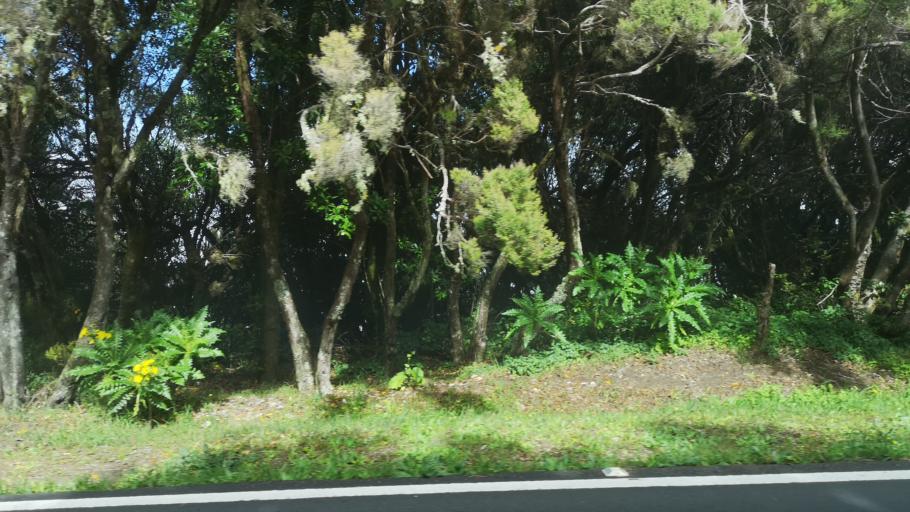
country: ES
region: Canary Islands
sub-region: Provincia de Santa Cruz de Tenerife
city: Alajero
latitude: 28.1076
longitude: -17.2390
